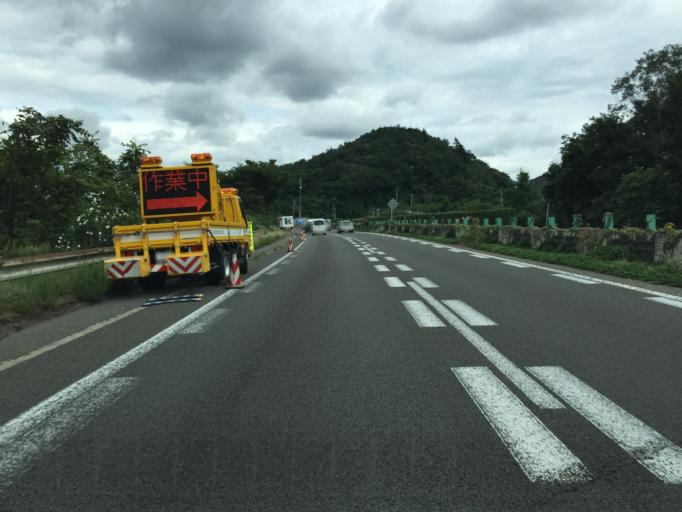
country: JP
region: Miyagi
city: Shiroishi
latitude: 37.9387
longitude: 140.6111
